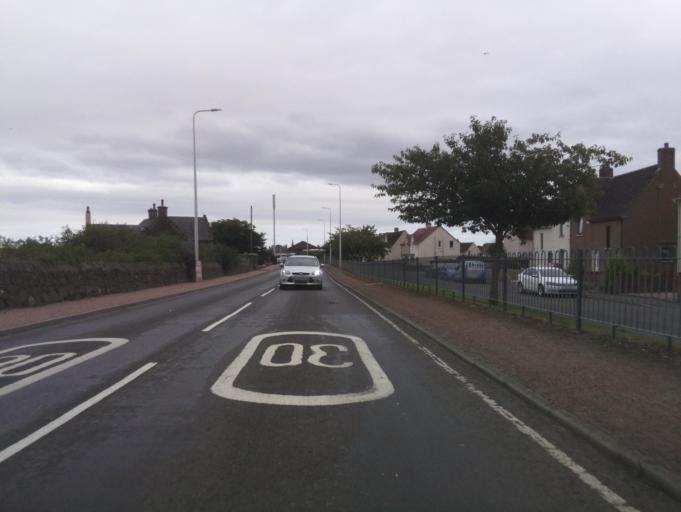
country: GB
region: Scotland
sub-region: Fife
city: Leslie
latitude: 56.2020
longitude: -3.2238
